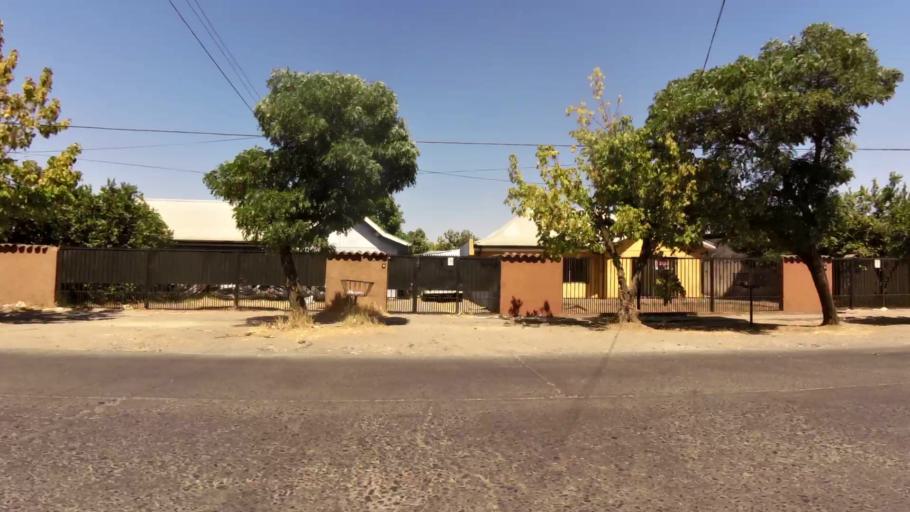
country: CL
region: Maule
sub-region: Provincia de Talca
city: Talca
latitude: -35.4145
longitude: -71.6543
